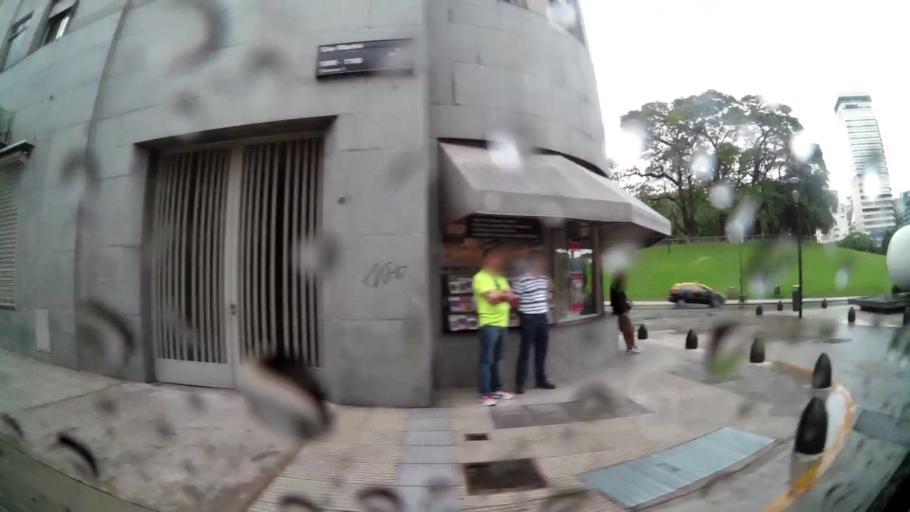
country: AR
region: Buenos Aires F.D.
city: Retiro
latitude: -34.5951
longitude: -58.3744
